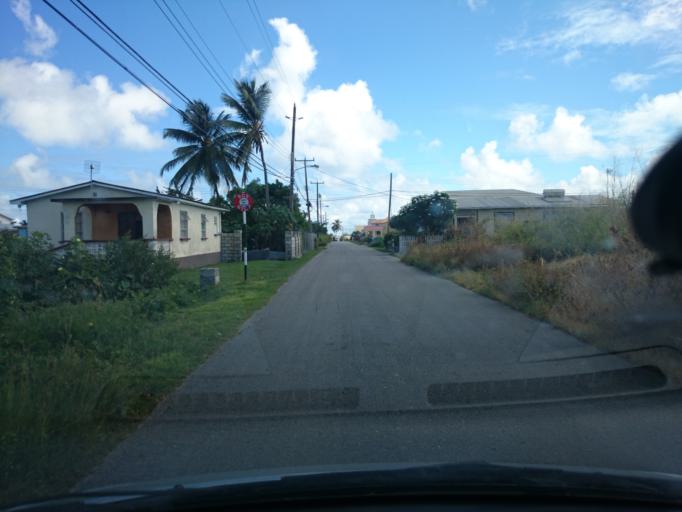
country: BB
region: Christ Church
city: Oistins
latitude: 13.0508
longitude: -59.5217
